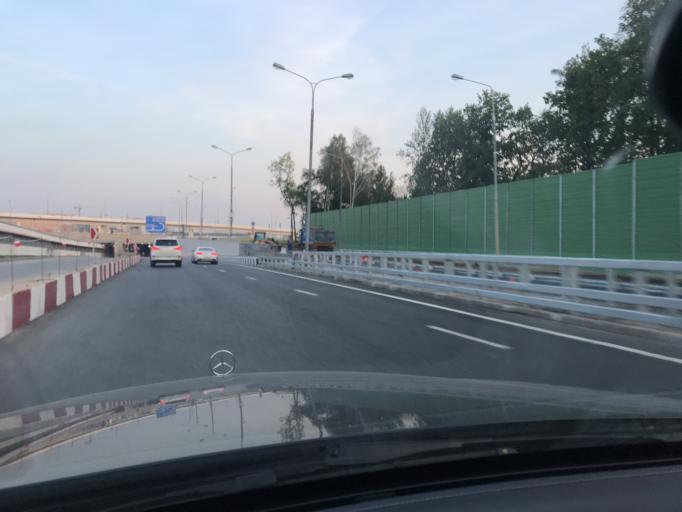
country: RU
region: Moskovskaya
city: Kommunarka
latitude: 55.5747
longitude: 37.4519
